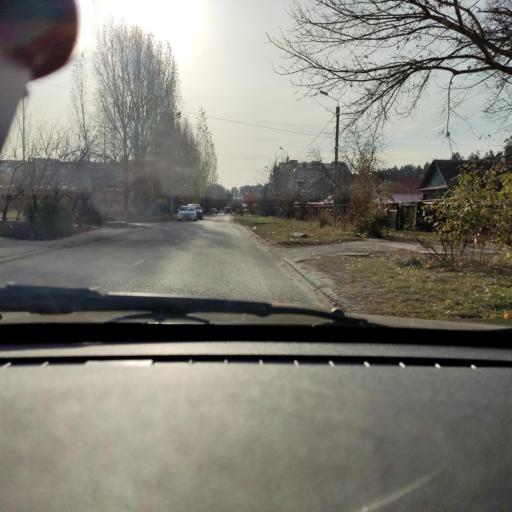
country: RU
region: Samara
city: Tol'yatti
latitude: 53.5310
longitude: 49.3897
